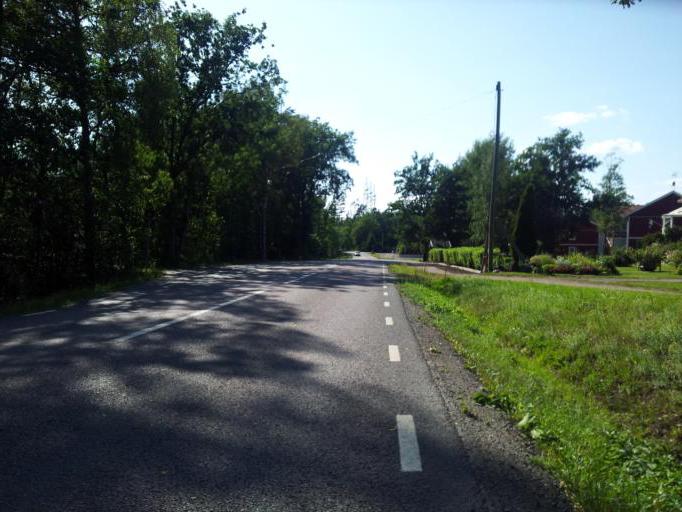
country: SE
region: Stockholm
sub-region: Norrtalje Kommun
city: Nykvarn
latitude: 59.8776
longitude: 18.0272
